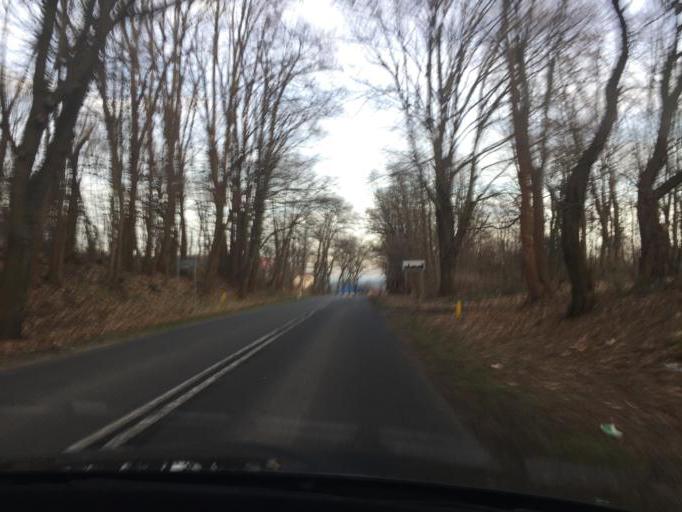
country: PL
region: Lubusz
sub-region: Powiat zarski
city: Brody
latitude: 51.7817
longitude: 14.7593
